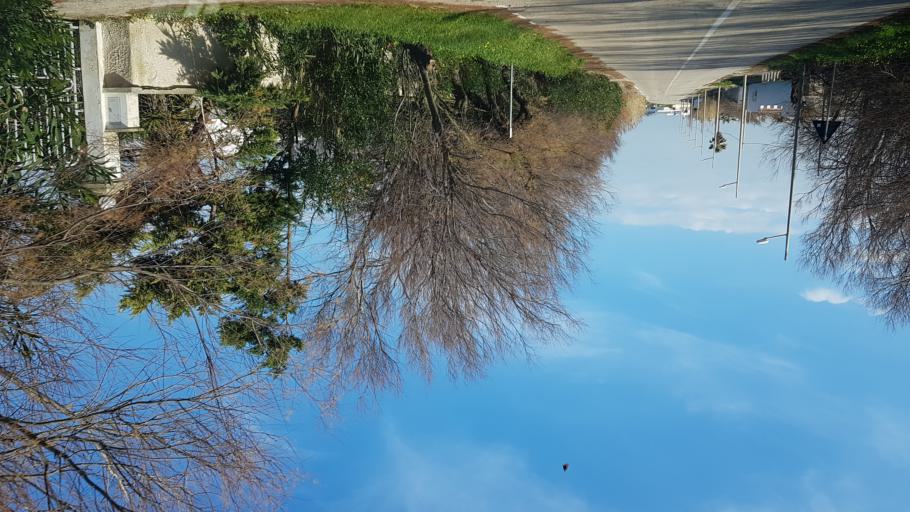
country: IT
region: Apulia
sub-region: Provincia di Brindisi
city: Brindisi
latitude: 40.6917
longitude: 17.8361
